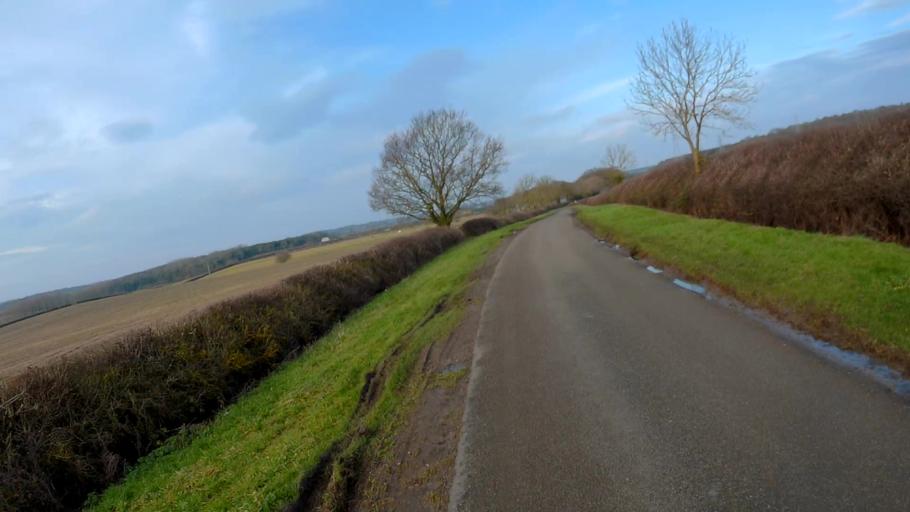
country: GB
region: England
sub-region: Lincolnshire
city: Bourne
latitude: 52.7564
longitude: -0.4185
